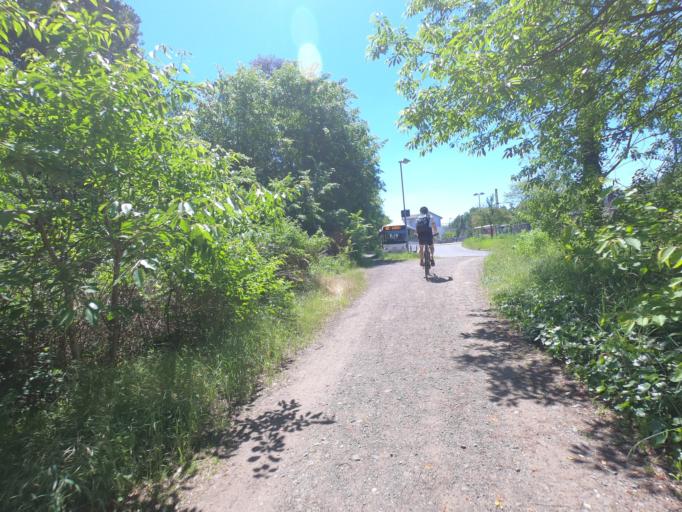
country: DE
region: Hesse
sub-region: Regierungsbezirk Darmstadt
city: Neu Isenburg
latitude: 50.0543
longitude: 8.6664
